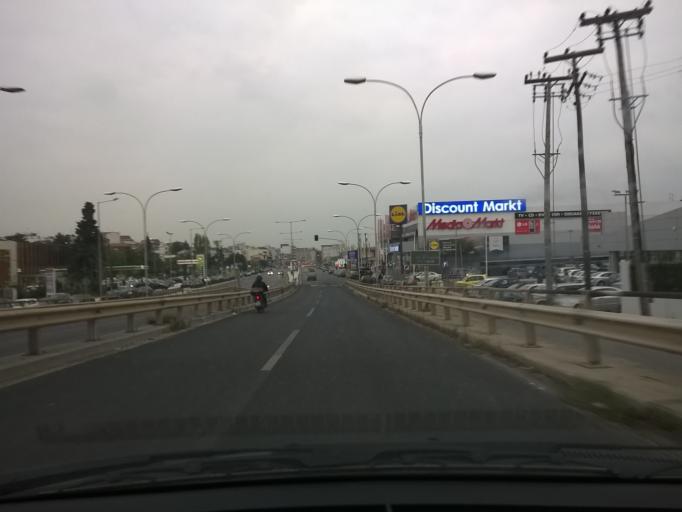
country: GR
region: Central Macedonia
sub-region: Nomos Thessalonikis
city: Stavroupoli
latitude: 40.6758
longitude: 22.9387
